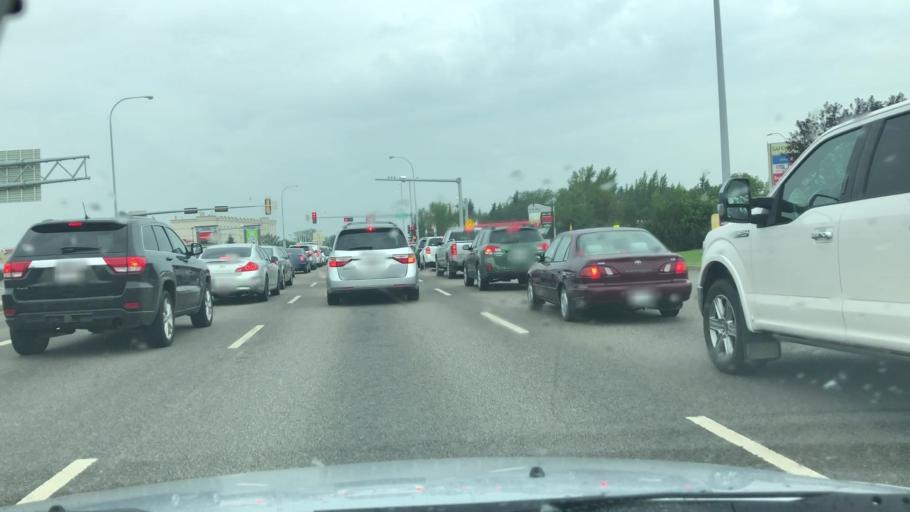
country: CA
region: Alberta
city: St. Albert
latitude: 53.6209
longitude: -113.6082
